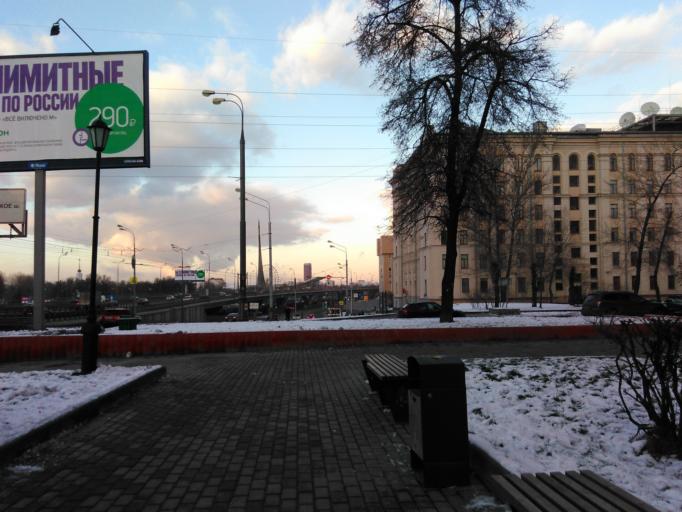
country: RU
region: Moscow
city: Ostankinskiy
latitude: 55.8162
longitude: 37.6392
